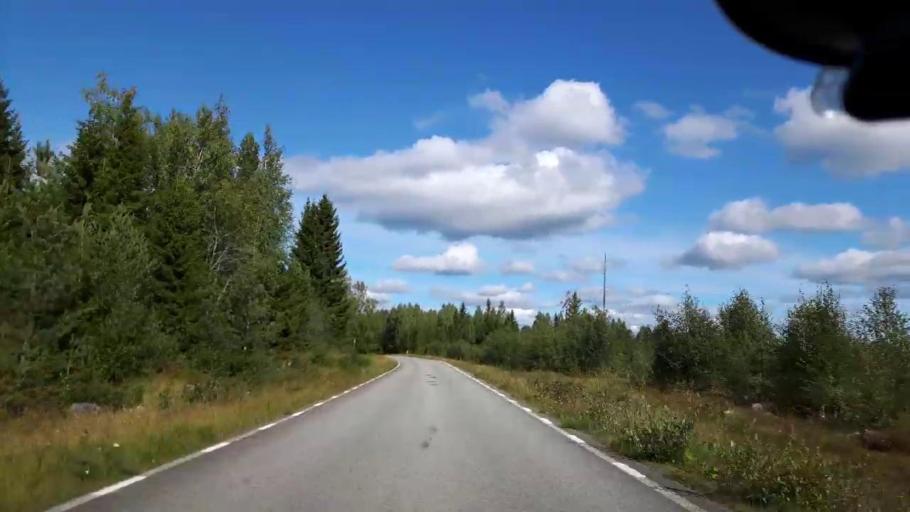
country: SE
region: Jaemtland
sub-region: OEstersunds Kommun
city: Brunflo
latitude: 63.2093
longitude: 15.2485
